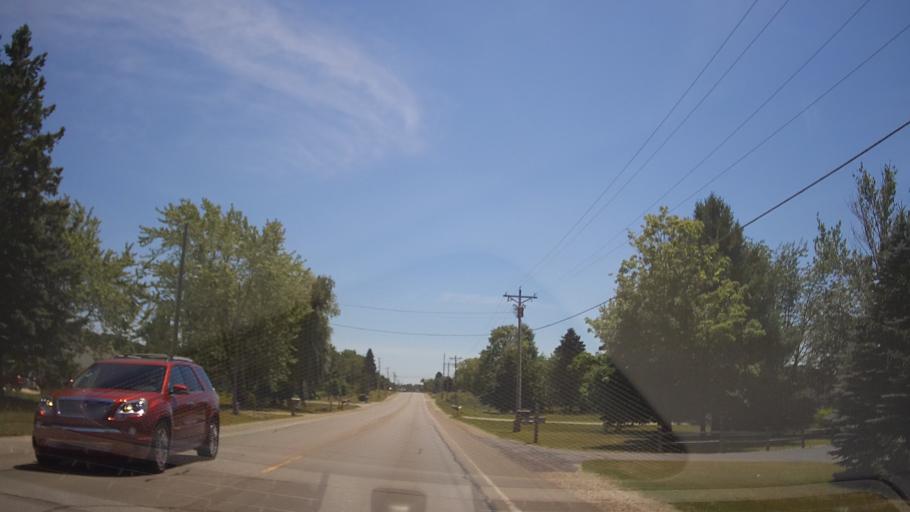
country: US
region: Michigan
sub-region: Grand Traverse County
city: Traverse City
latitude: 44.6722
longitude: -85.6900
